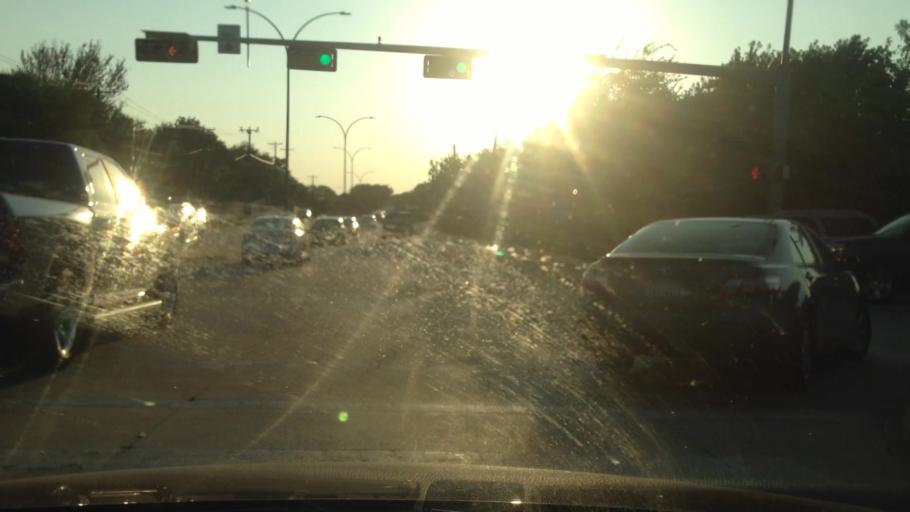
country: US
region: Texas
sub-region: Tarrant County
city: Kennedale
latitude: 32.6493
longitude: -97.1754
